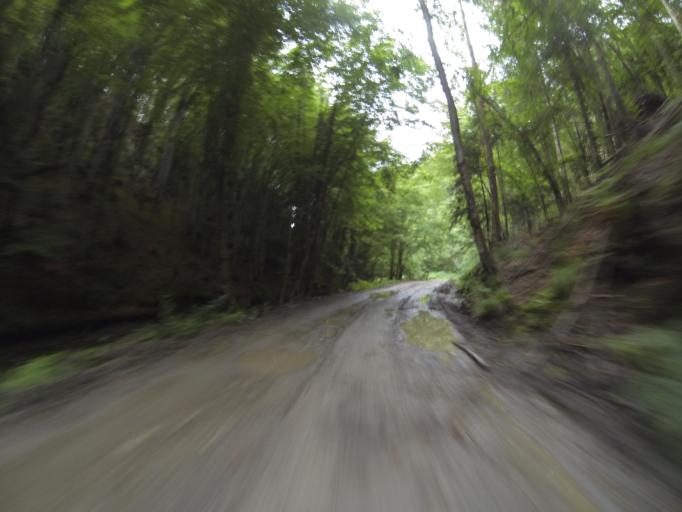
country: RO
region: Brasov
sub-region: Comuna Sinca Veche
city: Sinca Veche
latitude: 45.6880
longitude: 25.1511
